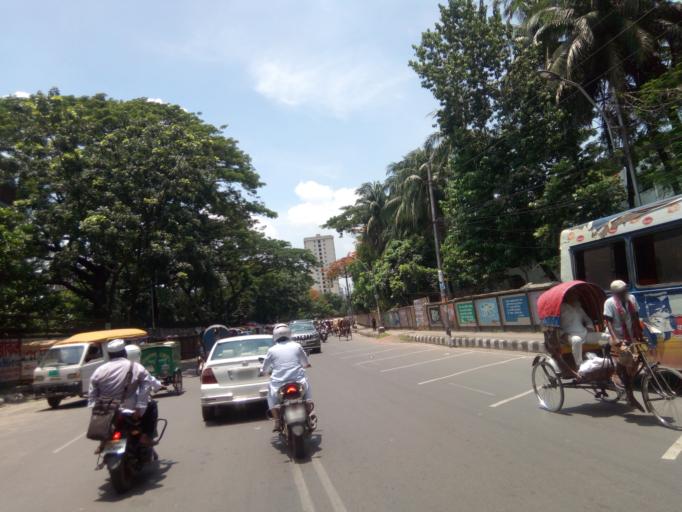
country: BD
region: Dhaka
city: Azimpur
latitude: 23.7301
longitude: 90.3874
